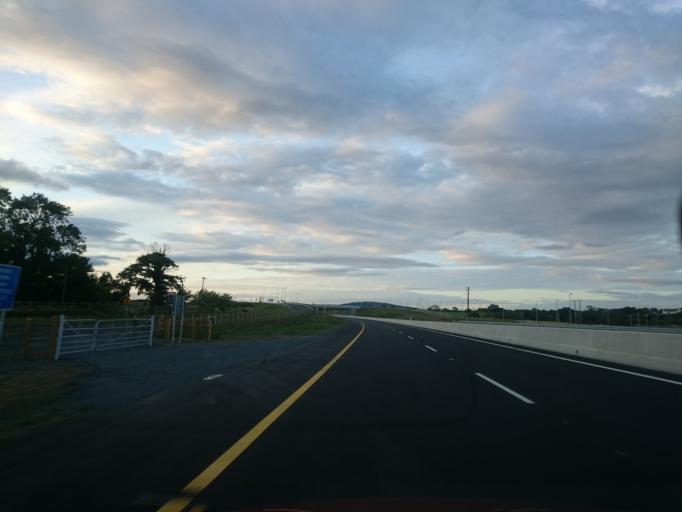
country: IE
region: Leinster
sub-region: Wicklow
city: Arklow
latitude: 52.8531
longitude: -6.1066
